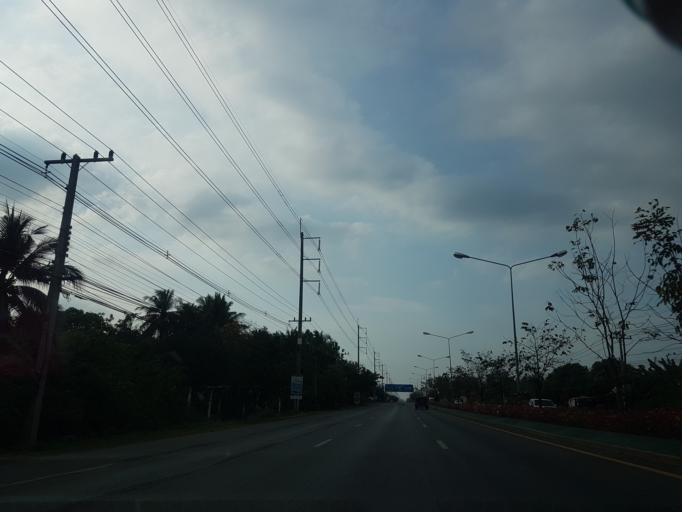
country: TH
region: Sara Buri
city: Phra Phutthabat
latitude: 14.7523
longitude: 100.7408
